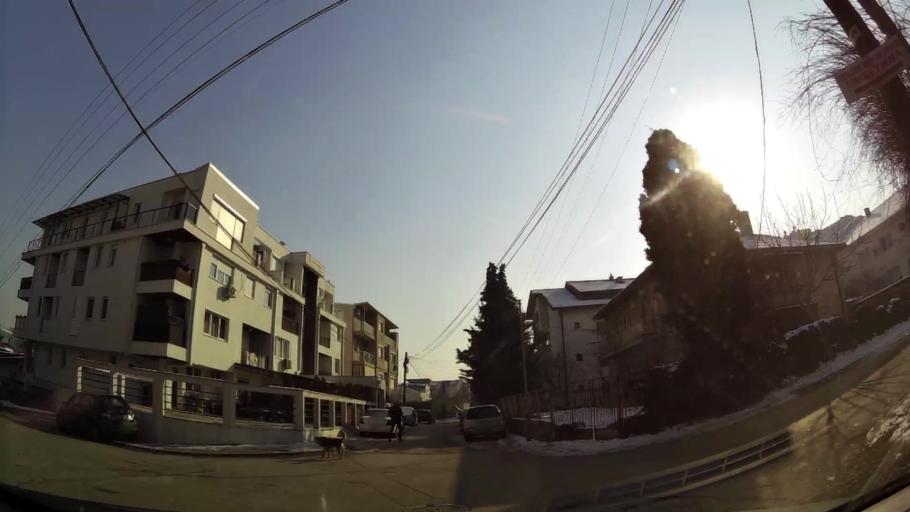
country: MK
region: Karpos
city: Skopje
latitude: 41.9822
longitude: 21.4297
